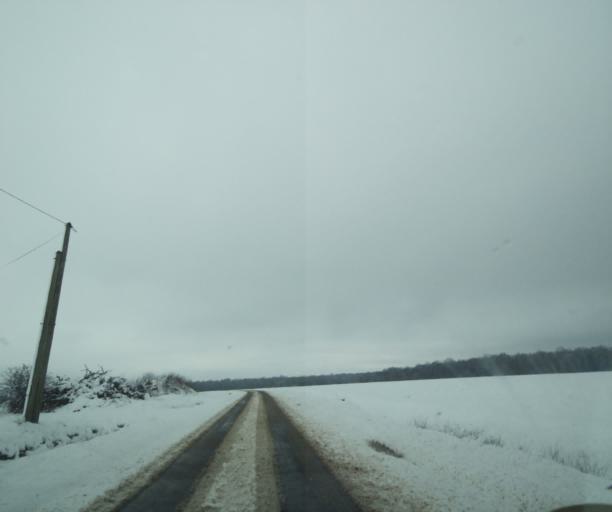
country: FR
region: Champagne-Ardenne
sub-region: Departement de la Haute-Marne
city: Montier-en-Der
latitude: 48.5129
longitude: 4.7685
